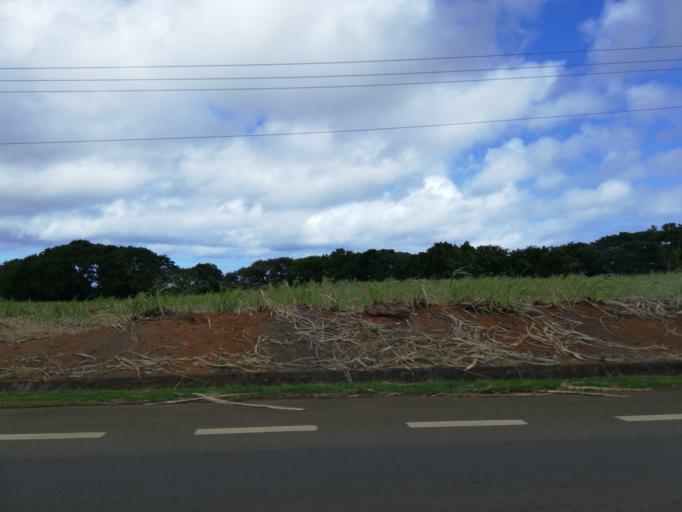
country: MU
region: Grand Port
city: Plaine Magnien
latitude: -20.4188
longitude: 57.6685
